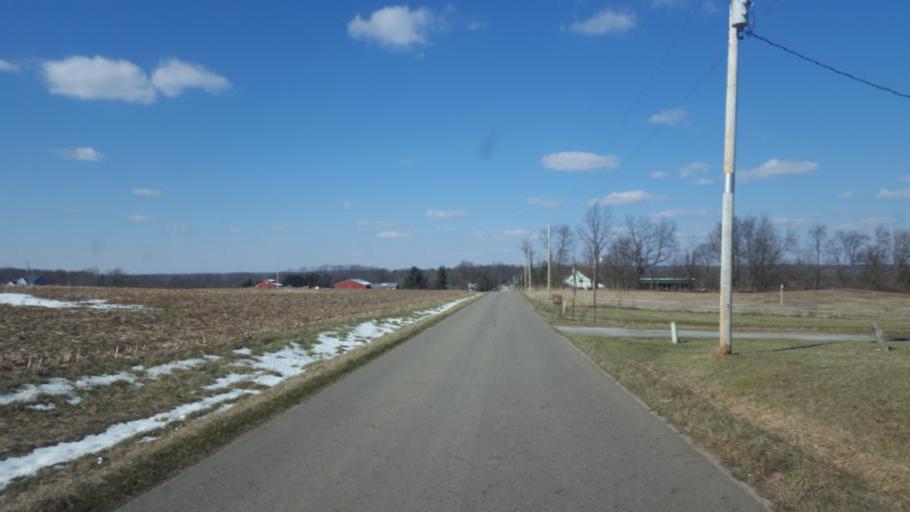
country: US
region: Ohio
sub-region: Knox County
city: Fredericktown
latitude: 40.4483
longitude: -82.6779
